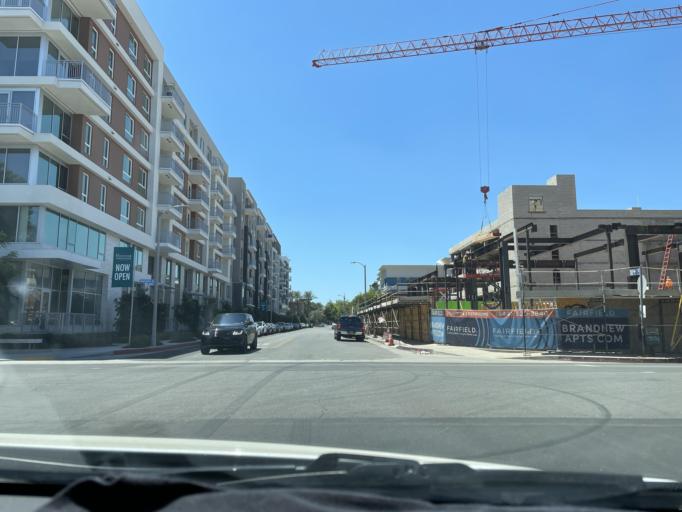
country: US
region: California
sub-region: Los Angeles County
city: Canoga Park
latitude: 34.1912
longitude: -118.5905
